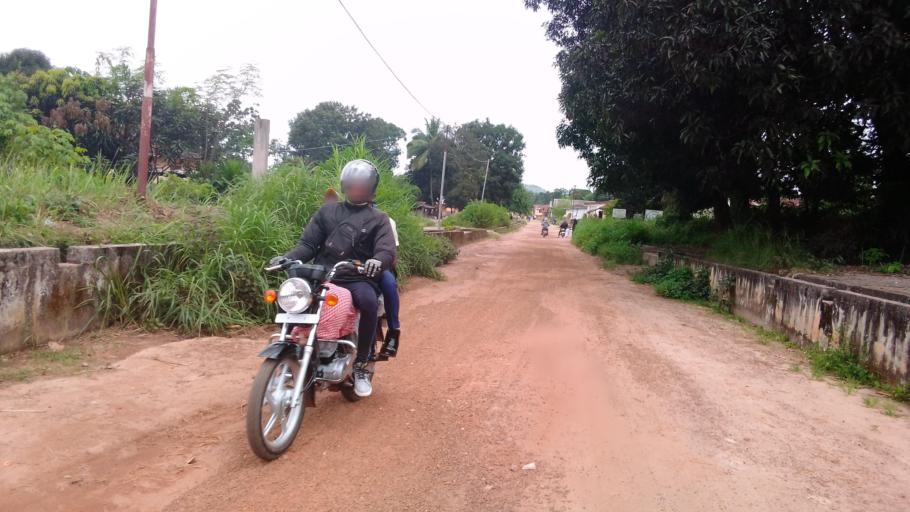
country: SL
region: Northern Province
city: Makeni
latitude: 8.8743
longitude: -12.0373
